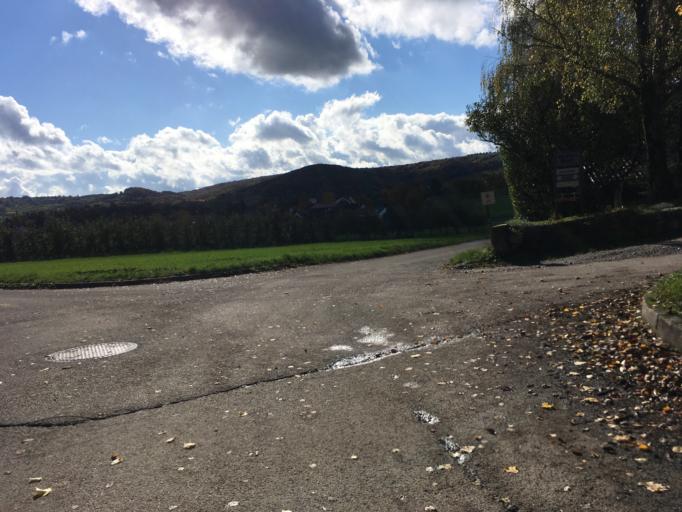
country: DE
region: Baden-Wuerttemberg
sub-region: Regierungsbezirk Stuttgart
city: Pfedelbach
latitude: 49.1840
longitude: 9.4821
